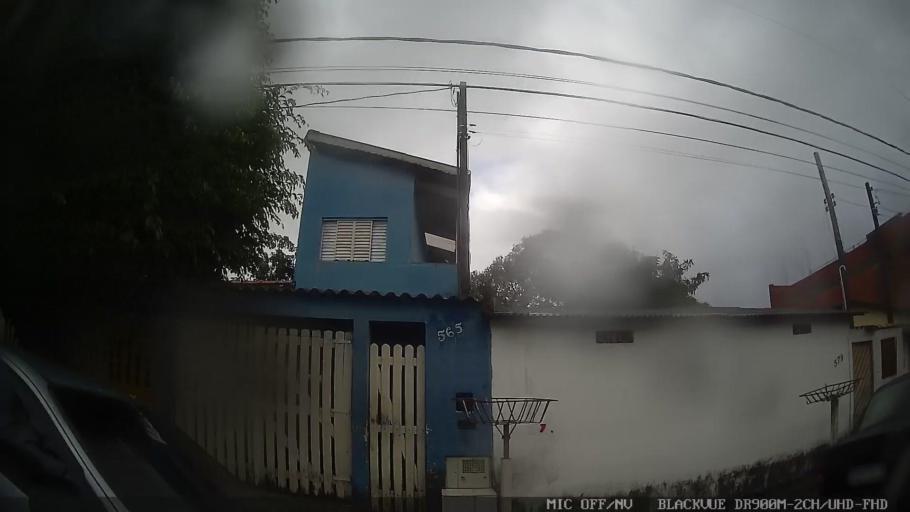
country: BR
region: Sao Paulo
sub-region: Itanhaem
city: Itanhaem
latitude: -24.1855
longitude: -46.8124
